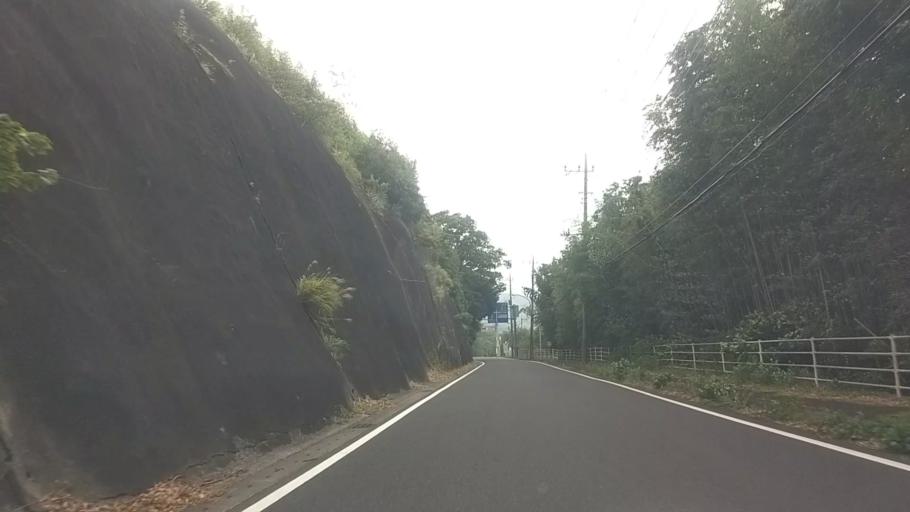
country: JP
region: Chiba
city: Kimitsu
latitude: 35.2515
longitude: 139.9932
